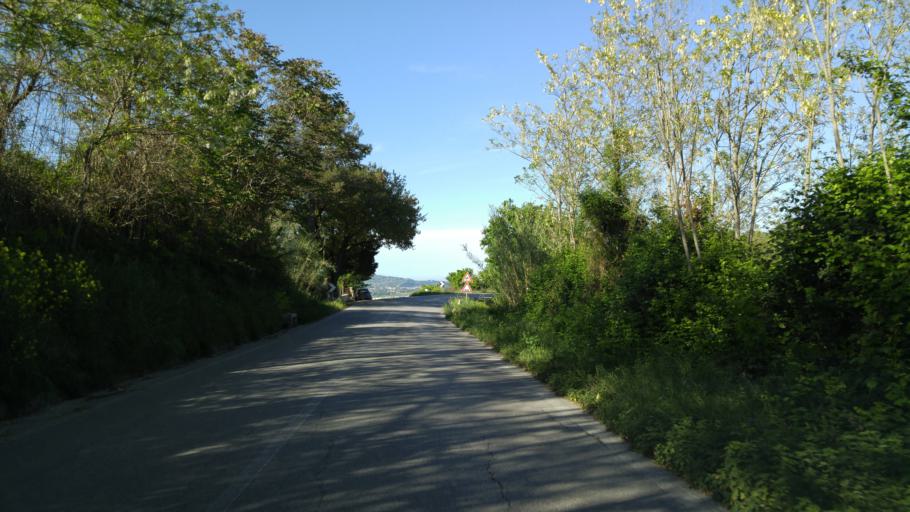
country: IT
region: The Marches
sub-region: Provincia di Pesaro e Urbino
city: Montemaggiore al Metauro
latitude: 43.7387
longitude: 12.9504
